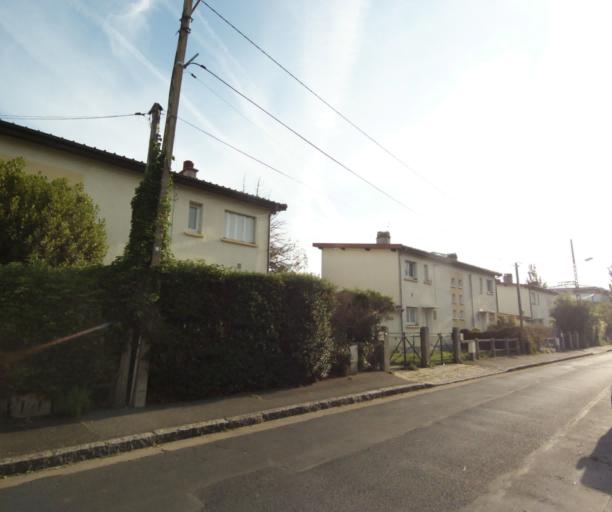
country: FR
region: Ile-de-France
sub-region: Departement du Val-d'Oise
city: Saint-Gratien
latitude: 48.9532
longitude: 2.2913
